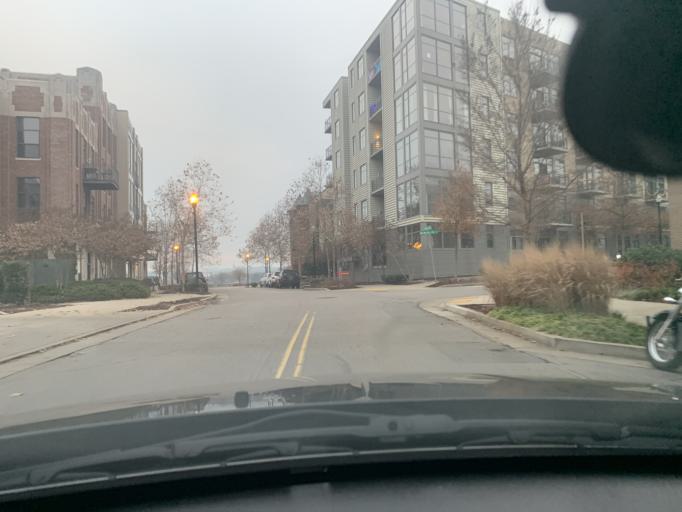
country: US
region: Tennessee
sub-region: Davidson County
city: Nashville
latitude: 36.1566
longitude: -86.7667
